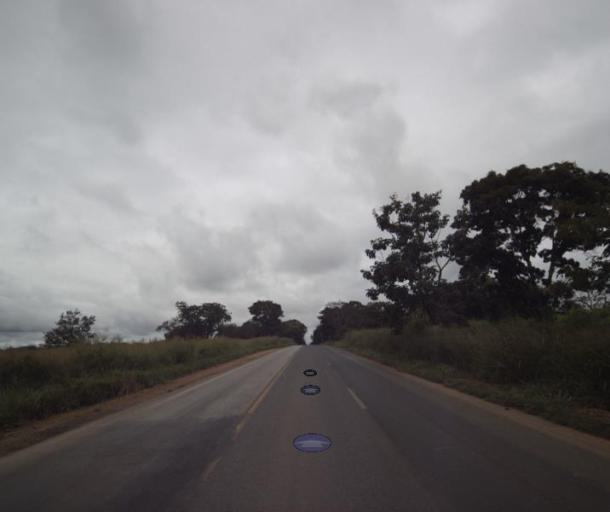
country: BR
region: Goias
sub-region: Uruacu
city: Uruacu
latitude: -14.5956
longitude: -49.1638
